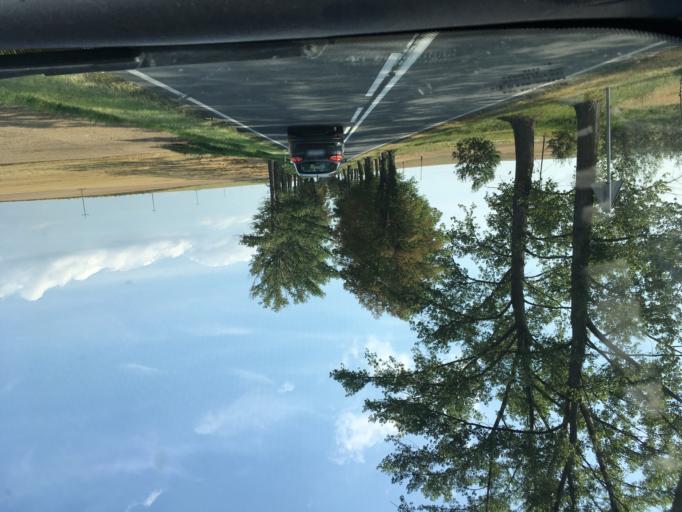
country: PL
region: Opole Voivodeship
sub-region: Powiat prudnicki
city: Laka Prudnicka
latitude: 50.3858
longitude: 17.5227
